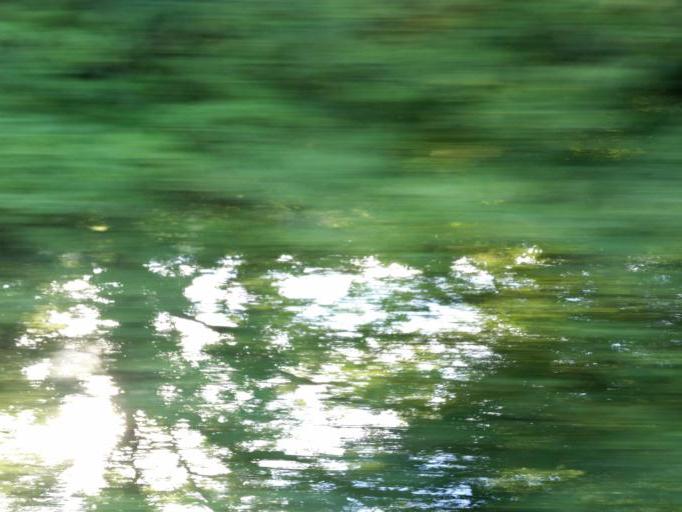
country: US
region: Tennessee
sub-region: Blount County
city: Eagleton Village
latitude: 35.8255
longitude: -83.9184
